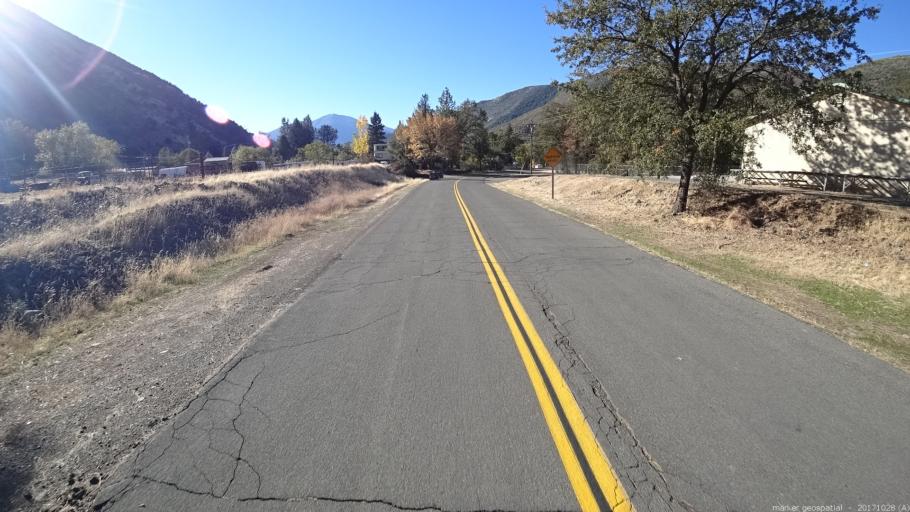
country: US
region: California
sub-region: Trinity County
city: Lewiston
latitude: 40.7060
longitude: -122.6351
